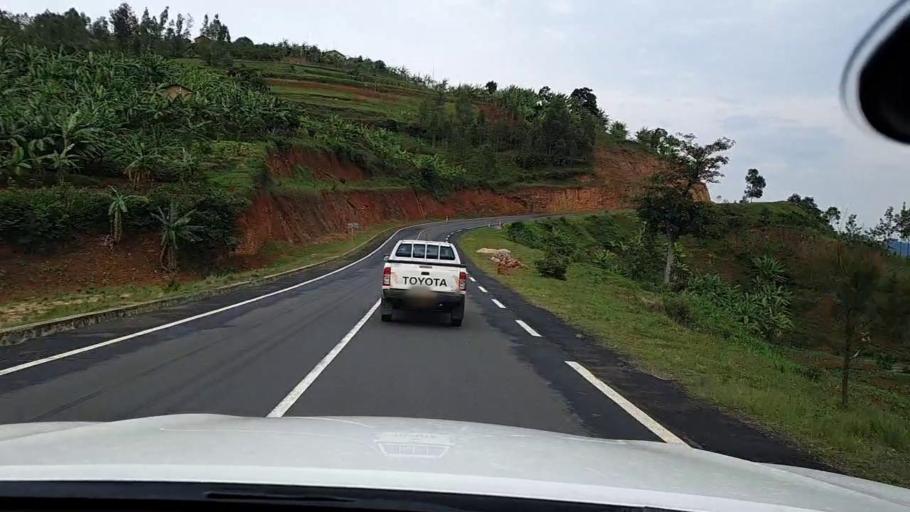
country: RW
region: Western Province
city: Kibuye
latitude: -2.1663
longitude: 29.2960
